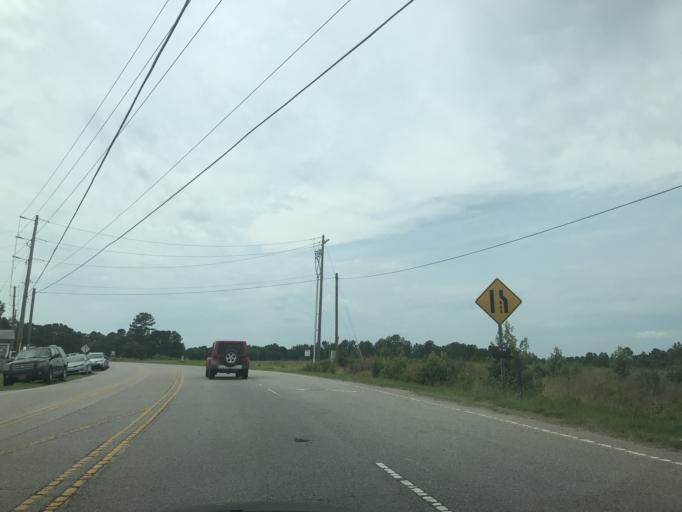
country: US
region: North Carolina
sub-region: Vance County
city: Henderson
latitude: 36.3378
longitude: -78.4419
